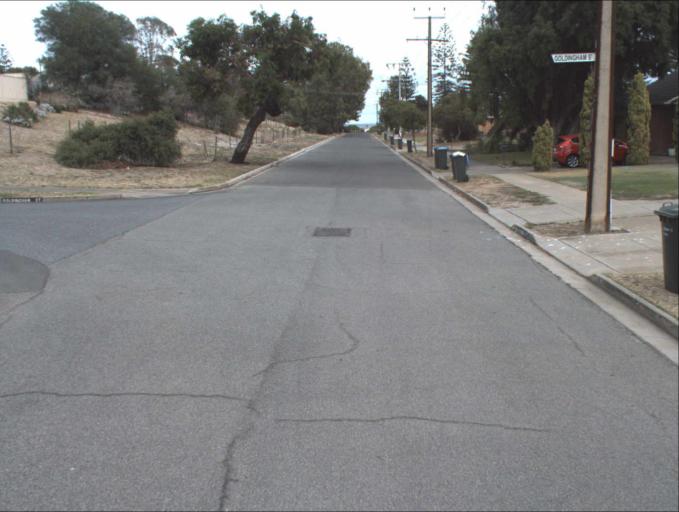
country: AU
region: South Australia
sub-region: Port Adelaide Enfield
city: Birkenhead
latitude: -34.8059
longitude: 138.4939
